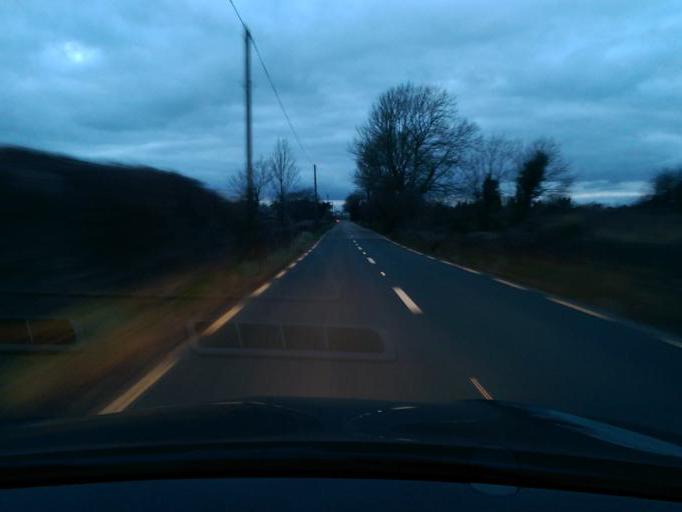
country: IE
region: Connaught
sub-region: County Galway
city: Portumna
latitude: 53.1561
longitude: -8.2696
